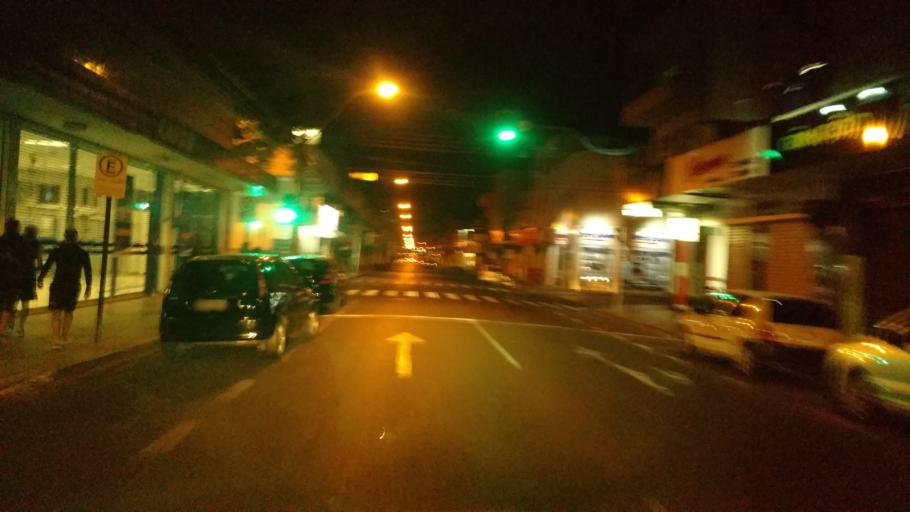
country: BR
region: Minas Gerais
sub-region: Uberlandia
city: Uberlandia
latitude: -18.9067
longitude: -48.2672
